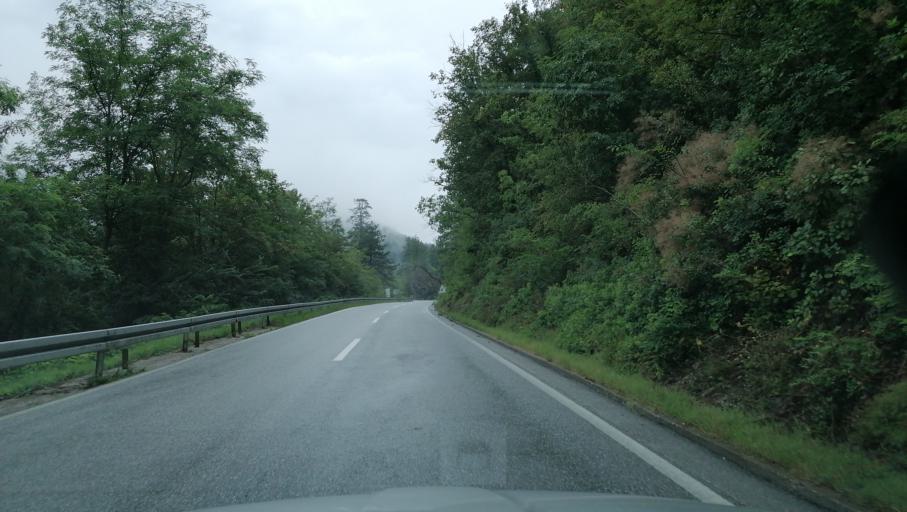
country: BA
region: Republika Srpska
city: Visegrad
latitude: 43.7820
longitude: 19.3518
